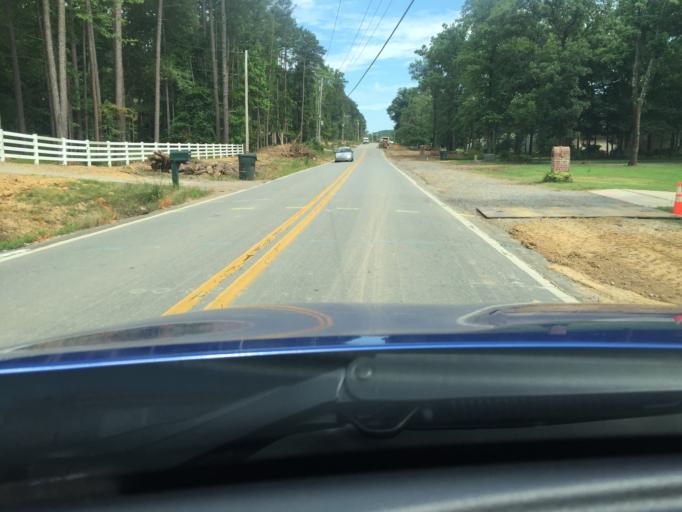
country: US
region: Arkansas
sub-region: Pulaski County
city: Maumelle
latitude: 34.8085
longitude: -92.4408
